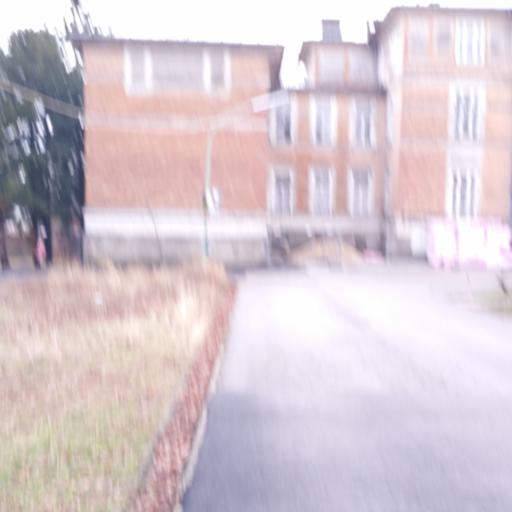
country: AT
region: Vienna
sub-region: Wien Stadt
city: Vienna
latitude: 48.2095
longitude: 16.2850
